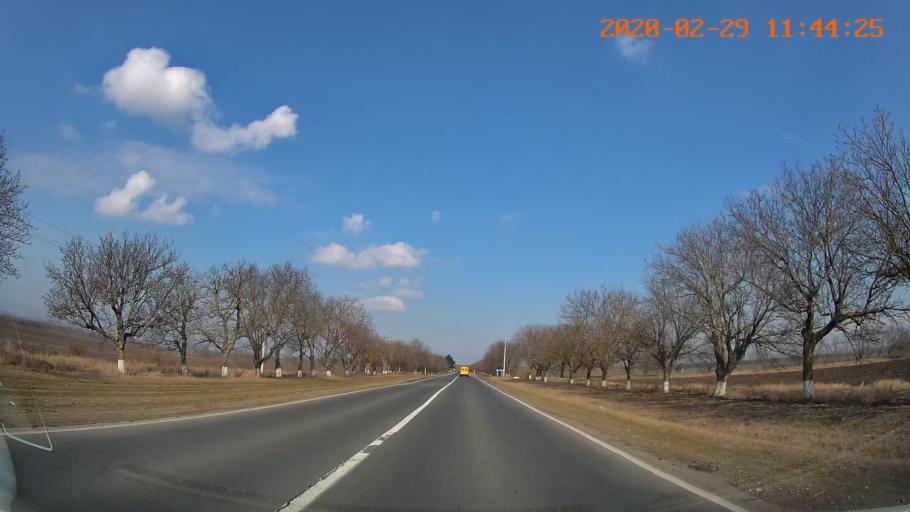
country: MD
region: Rezina
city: Saharna
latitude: 47.7112
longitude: 29.0008
